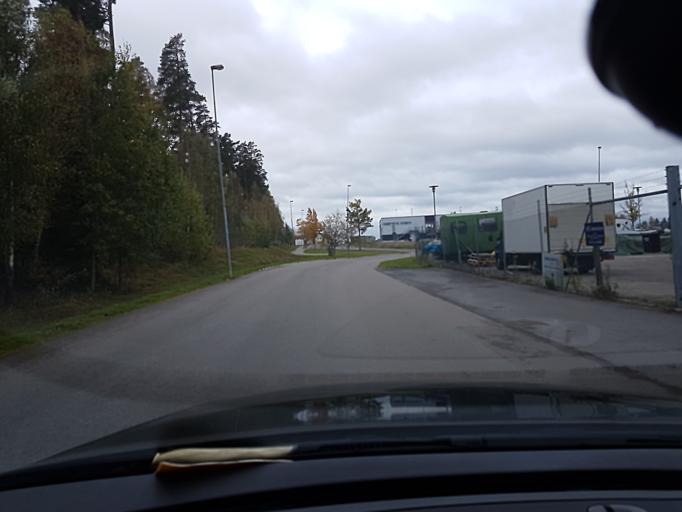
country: SE
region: Kronoberg
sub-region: Vaxjo Kommun
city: Vaexjoe
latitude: 56.9025
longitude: 14.8368
